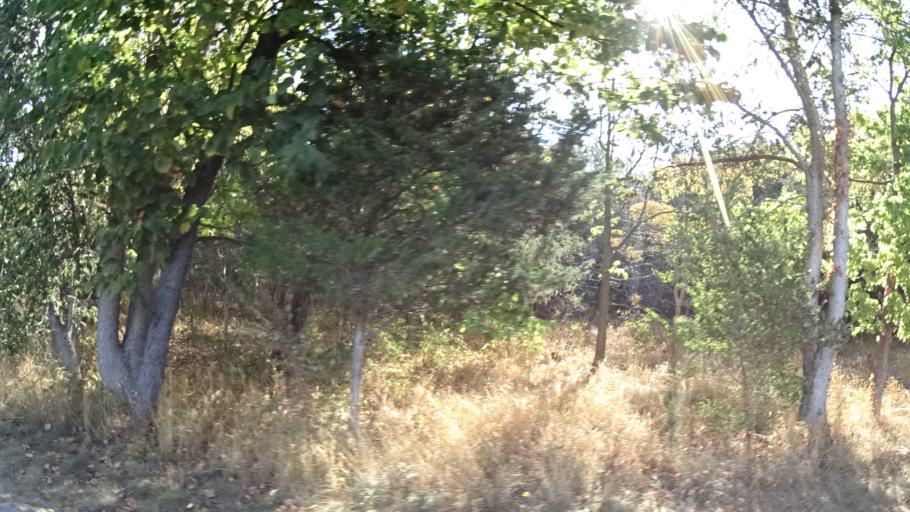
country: US
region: Ohio
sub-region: Erie County
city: Sandusky
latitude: 41.6110
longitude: -82.6887
